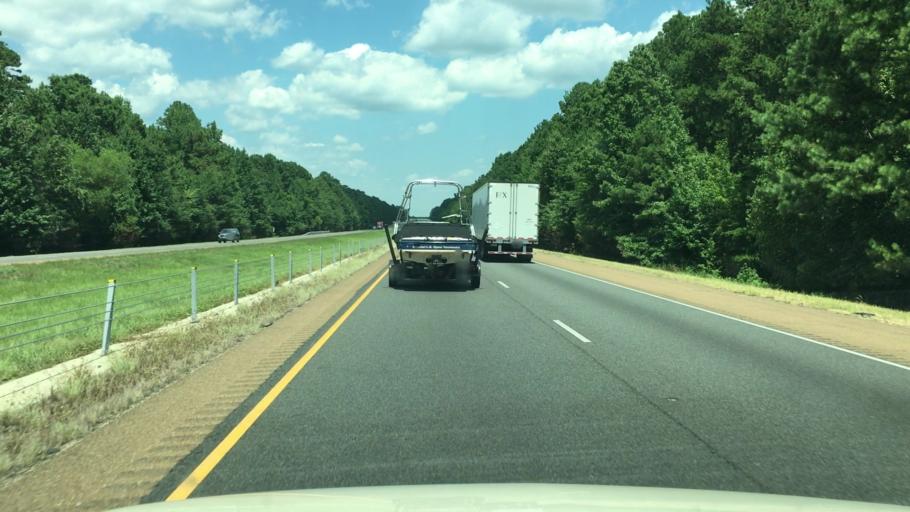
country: US
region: Arkansas
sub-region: Clark County
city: Gurdon
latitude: 33.9630
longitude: -93.2172
